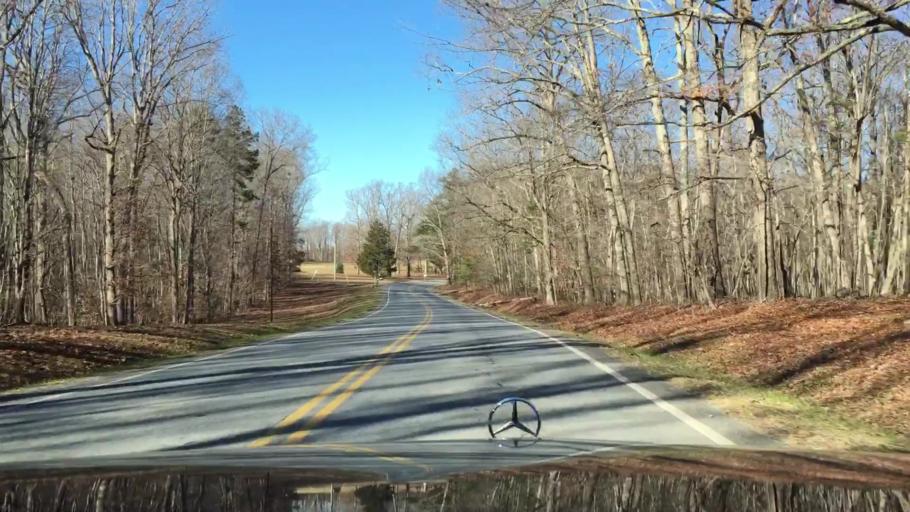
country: US
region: Virginia
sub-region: Pittsylvania County
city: Motley
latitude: 37.1712
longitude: -79.4070
